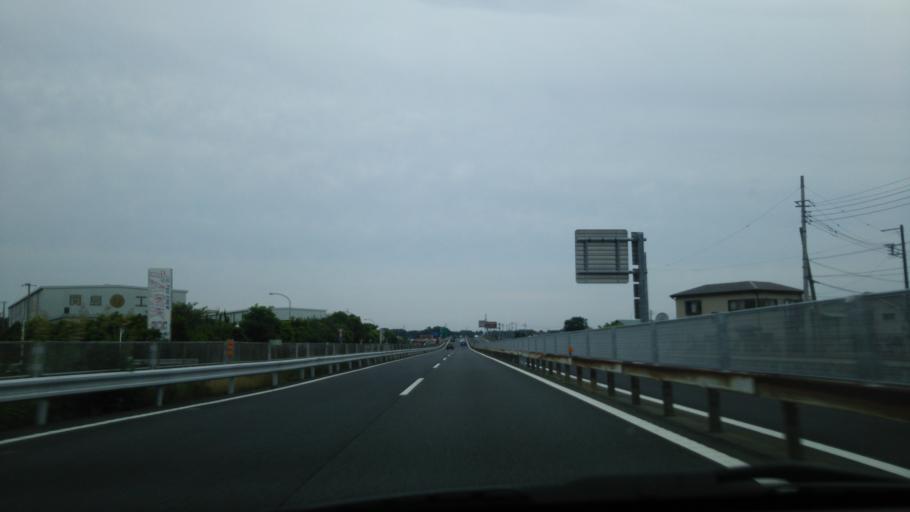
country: JP
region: Kanagawa
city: Isehara
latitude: 35.3656
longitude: 139.3082
